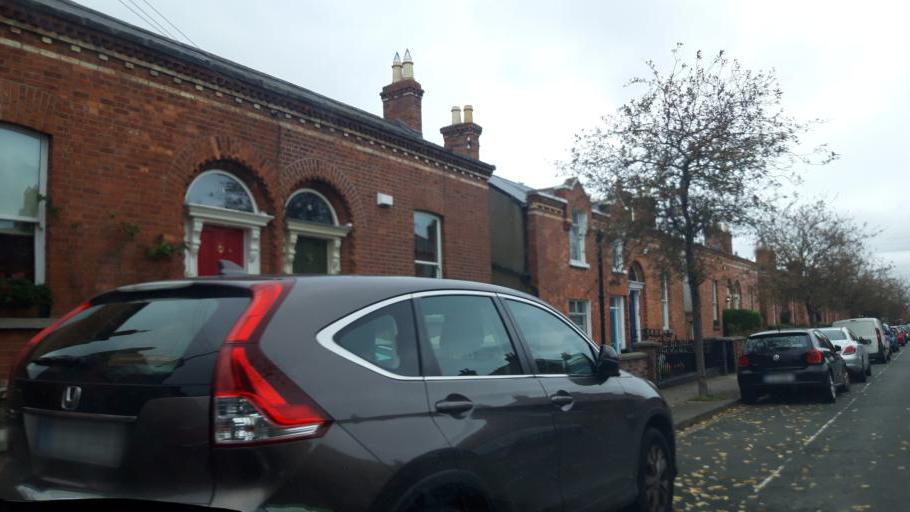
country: IE
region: Leinster
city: Rathmines
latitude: 53.3199
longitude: -6.2537
